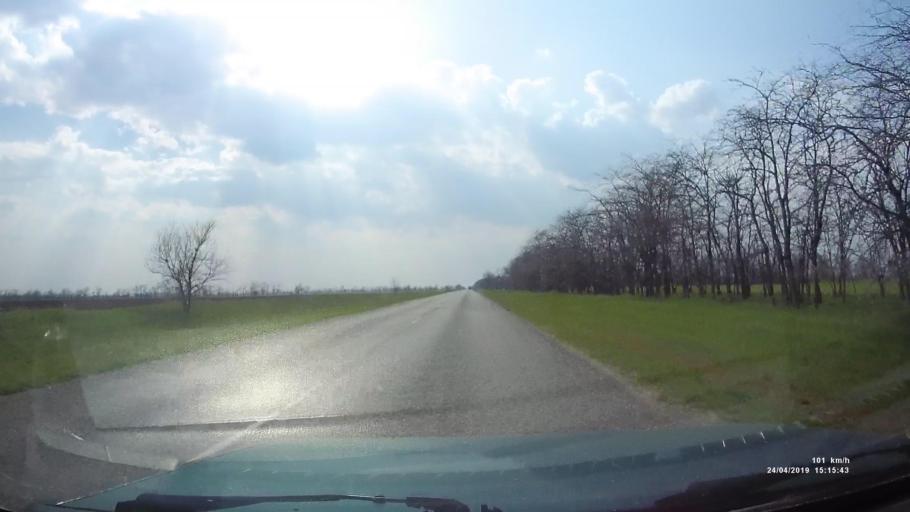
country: RU
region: Rostov
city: Remontnoye
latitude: 46.5465
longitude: 43.2291
